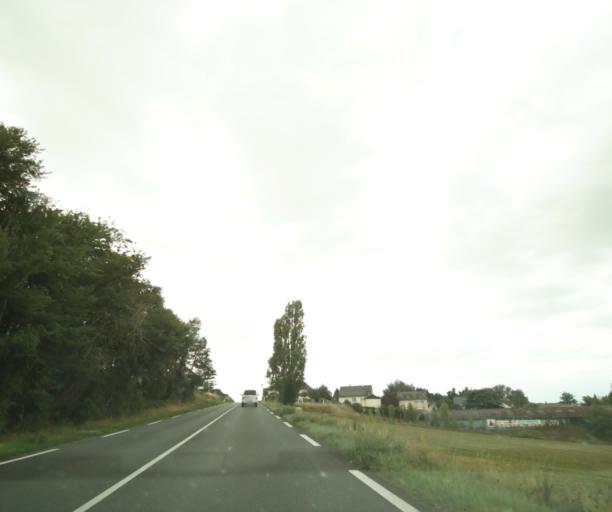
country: FR
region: Centre
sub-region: Departement d'Indre-et-Loire
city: Chambourg-sur-Indre
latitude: 47.1793
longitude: 0.9659
